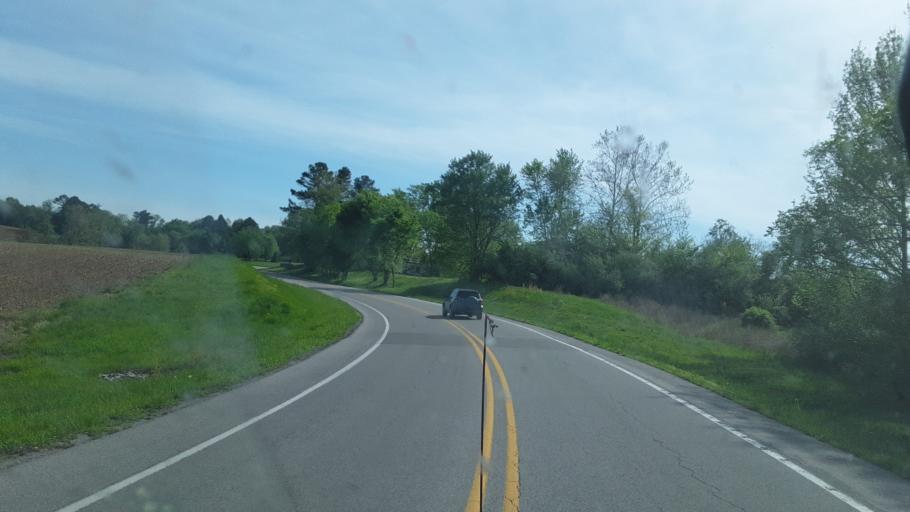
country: US
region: Illinois
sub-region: Jackson County
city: Carbondale
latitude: 37.6859
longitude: -89.2560
